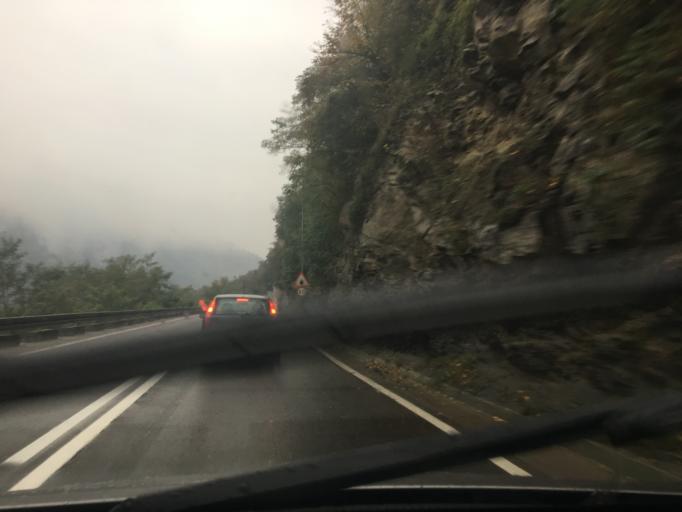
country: RS
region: Central Serbia
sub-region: Pcinjski Okrug
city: Vladicin Han
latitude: 42.7464
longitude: 22.0640
